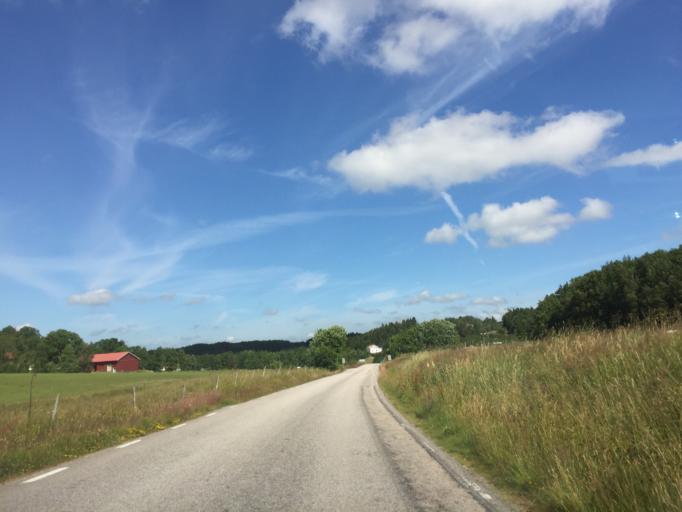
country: SE
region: Vaestra Goetaland
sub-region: Orust
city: Henan
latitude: 58.2896
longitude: 11.5812
